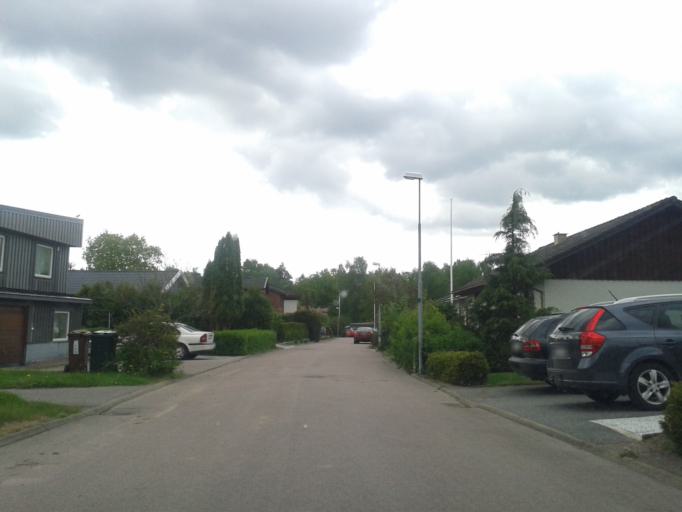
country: SE
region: Vaestra Goetaland
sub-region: Kungalvs Kommun
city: Kungalv
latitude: 57.8541
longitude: 11.9900
